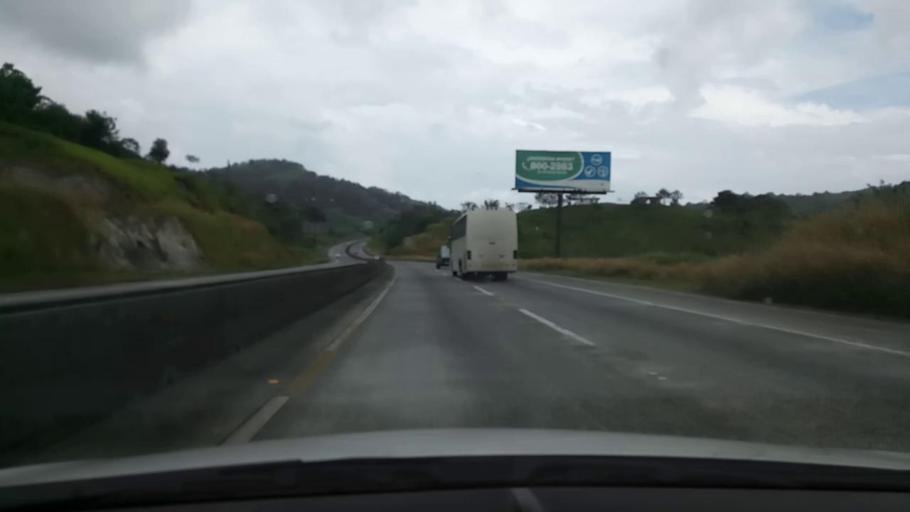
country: PA
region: Colon
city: Gatun
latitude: 9.2807
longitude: -79.7548
